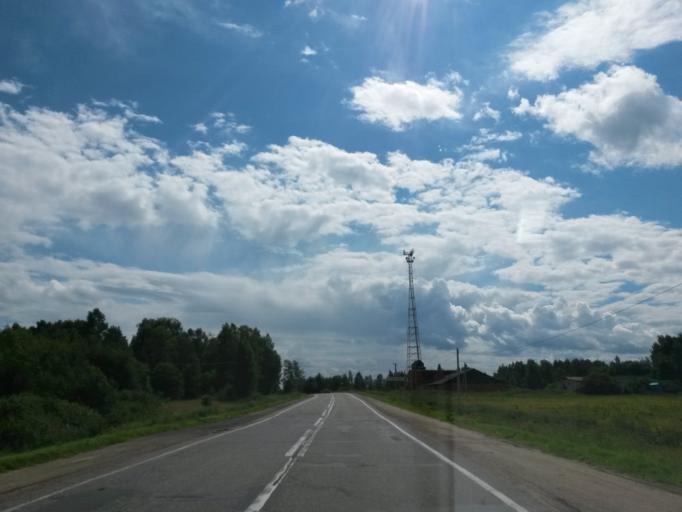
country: RU
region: Jaroslavl
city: Gavrilov-Yam
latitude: 57.3093
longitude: 39.9370
